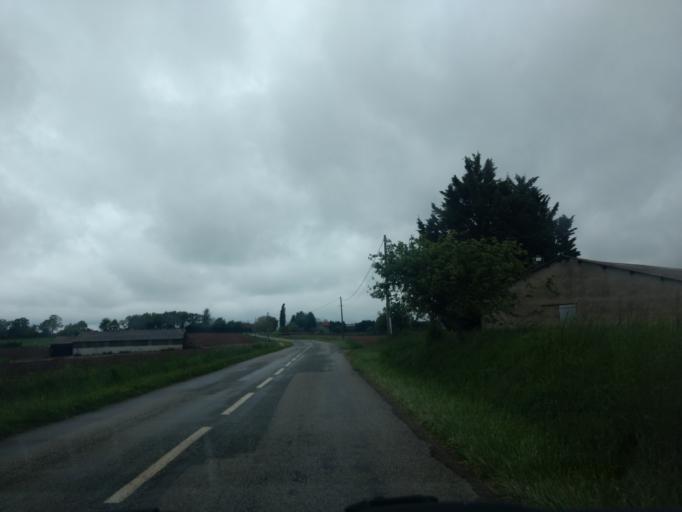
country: FR
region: Midi-Pyrenees
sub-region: Departement de l'Aveyron
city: Viviez
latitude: 44.5122
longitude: 2.1879
